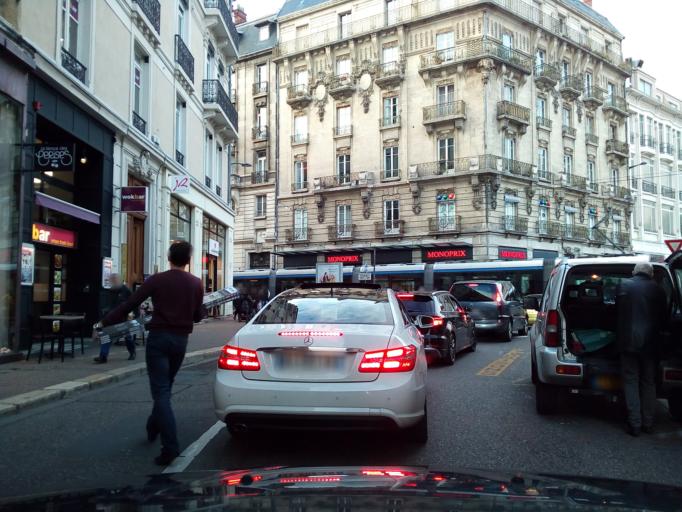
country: FR
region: Rhone-Alpes
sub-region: Departement de l'Isere
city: La Tronche
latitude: 45.1897
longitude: 5.7288
